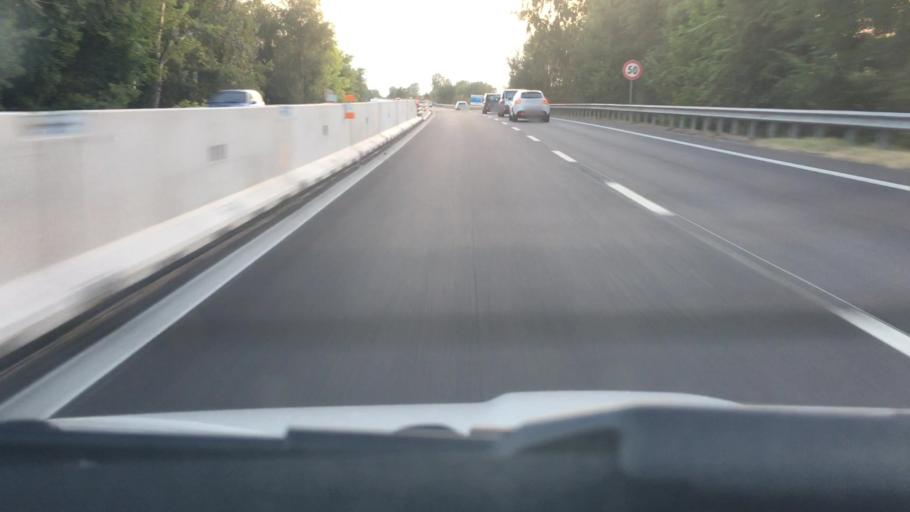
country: IT
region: Emilia-Romagna
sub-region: Provincia di Ferrara
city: Gaibanella-Sant'Edigio
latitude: 44.7984
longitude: 11.6491
